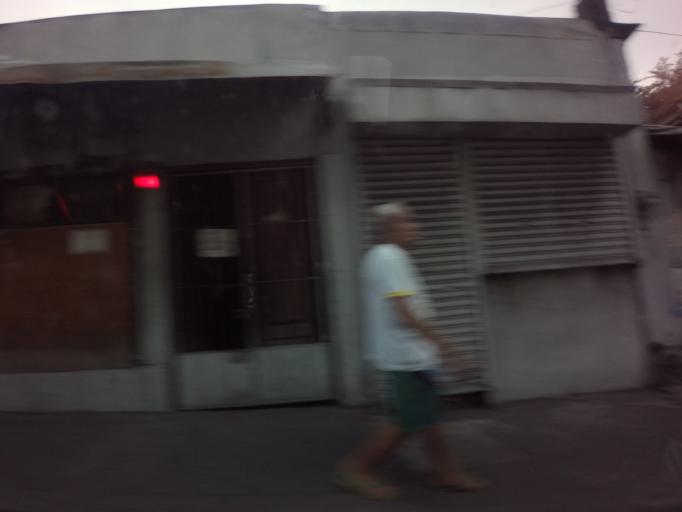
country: PH
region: Metro Manila
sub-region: Mandaluyong
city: Mandaluyong City
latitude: 14.5648
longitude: 121.0479
